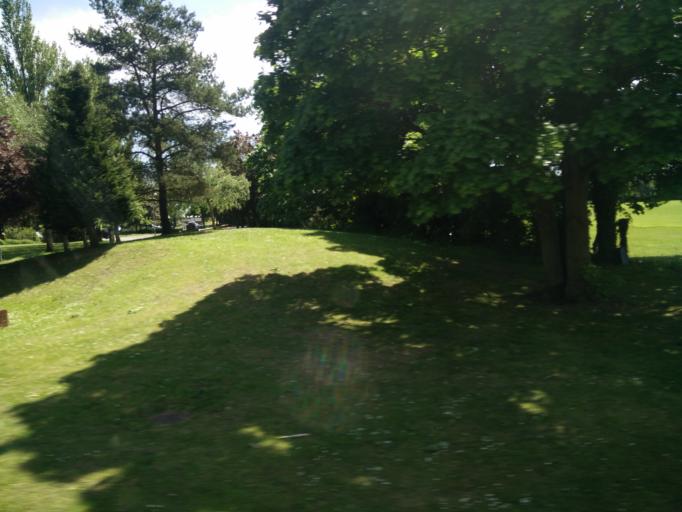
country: GB
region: England
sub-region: Hertfordshire
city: Letchworth Garden City
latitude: 51.9780
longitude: -0.2067
